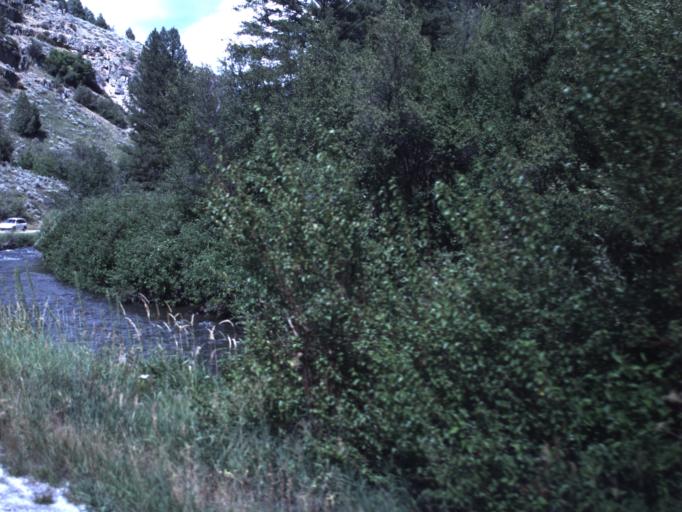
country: US
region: Utah
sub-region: Cache County
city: North Logan
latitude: 41.8175
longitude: -111.6174
